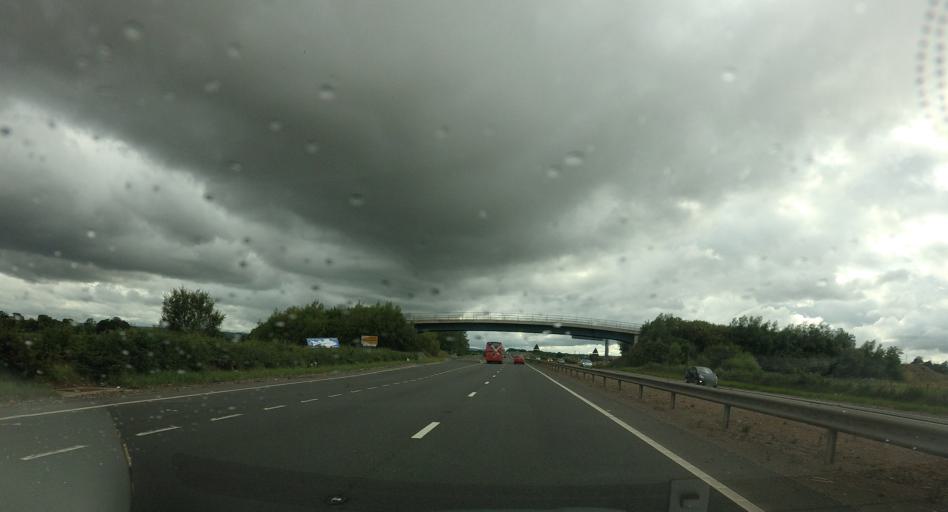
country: GB
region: Scotland
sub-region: Falkirk
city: Airth
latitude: 56.0585
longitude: -3.7461
